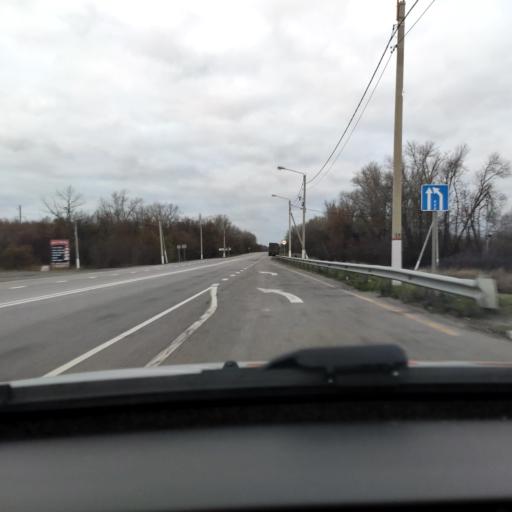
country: RU
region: Lipetsk
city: Khlevnoye
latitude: 52.2680
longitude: 39.1687
